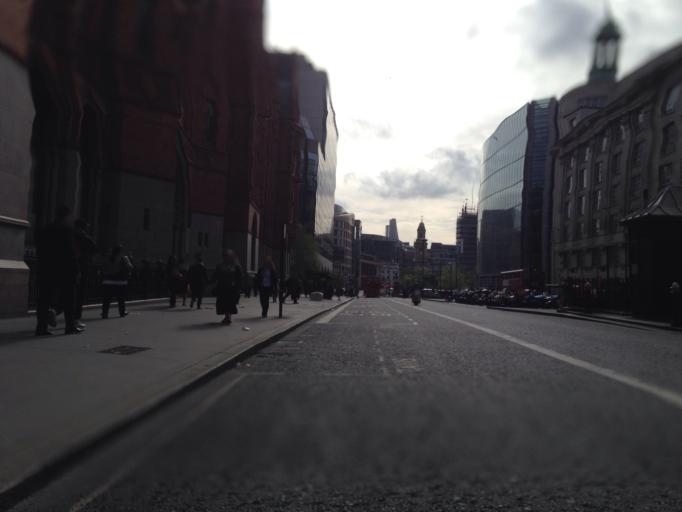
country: GB
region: England
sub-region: Greater London
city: Clerkenwell
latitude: 51.5181
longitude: -0.1104
